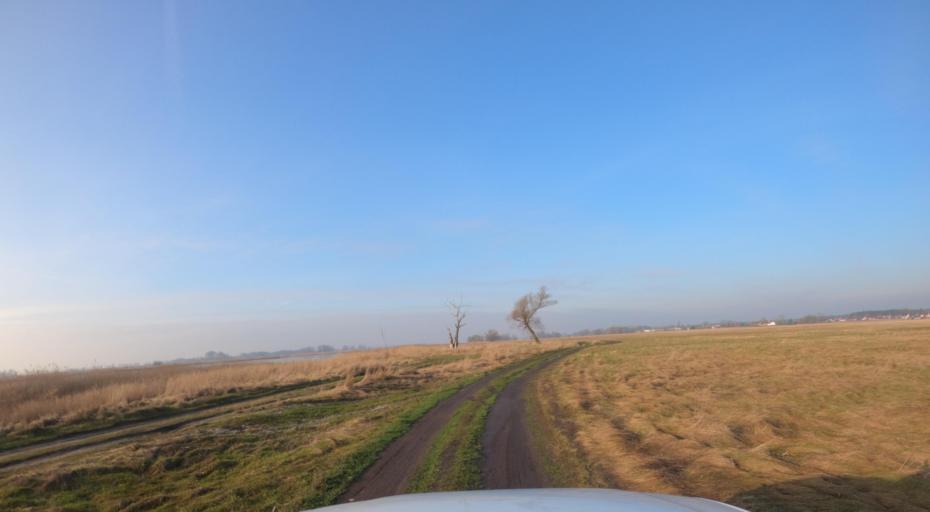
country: PL
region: Lubusz
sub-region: Powiat gorzowski
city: Kostrzyn nad Odra
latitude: 52.6130
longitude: 14.5937
